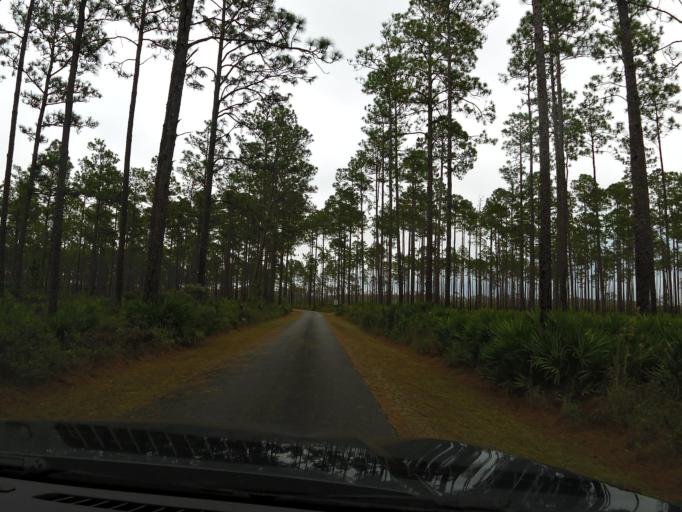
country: US
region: Georgia
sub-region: Charlton County
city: Folkston
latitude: 30.7085
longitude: -82.1601
